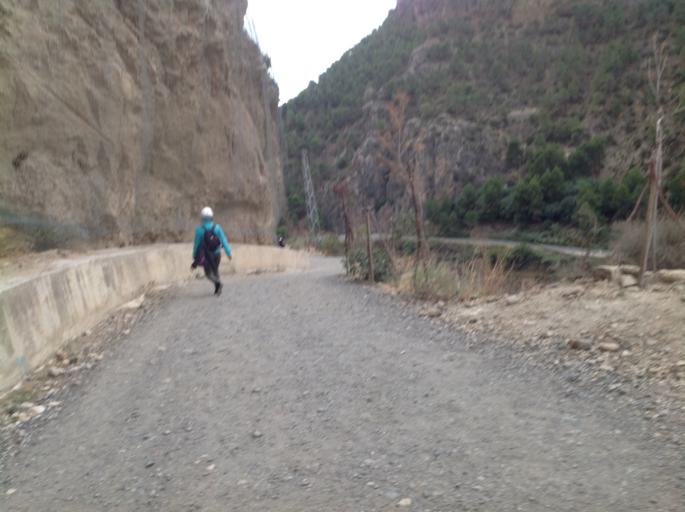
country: ES
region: Andalusia
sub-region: Provincia de Malaga
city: Carratraca
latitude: 36.9135
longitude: -4.7687
